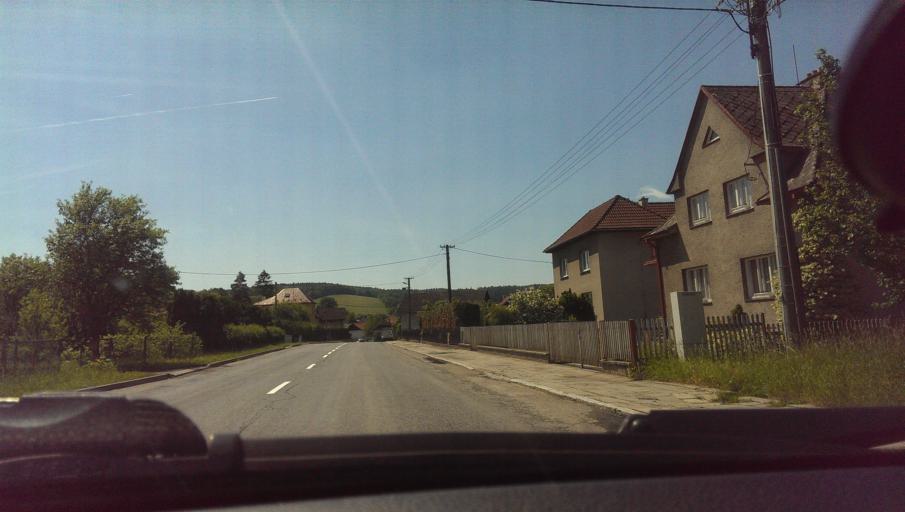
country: CZ
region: Zlin
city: Breznice
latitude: 49.1694
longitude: 17.6401
